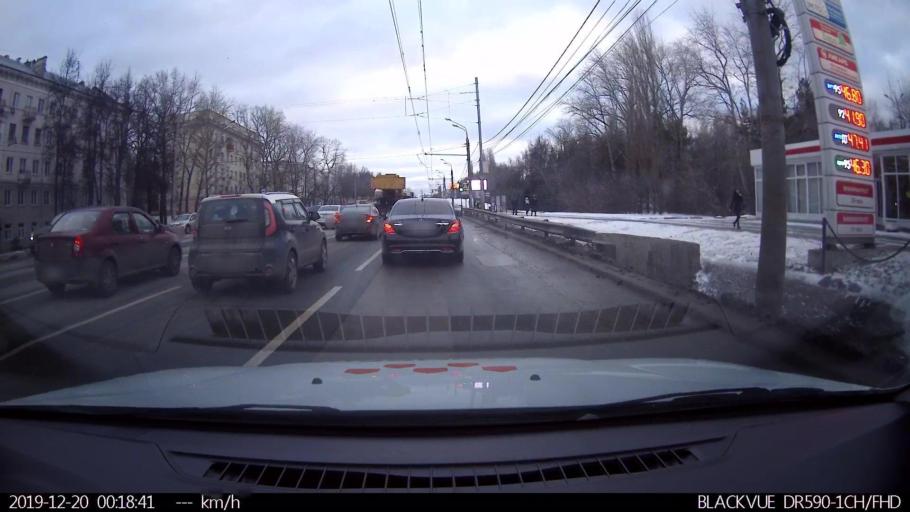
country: RU
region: Jaroslavl
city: Petrovsk
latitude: 56.8762
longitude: 39.4413
